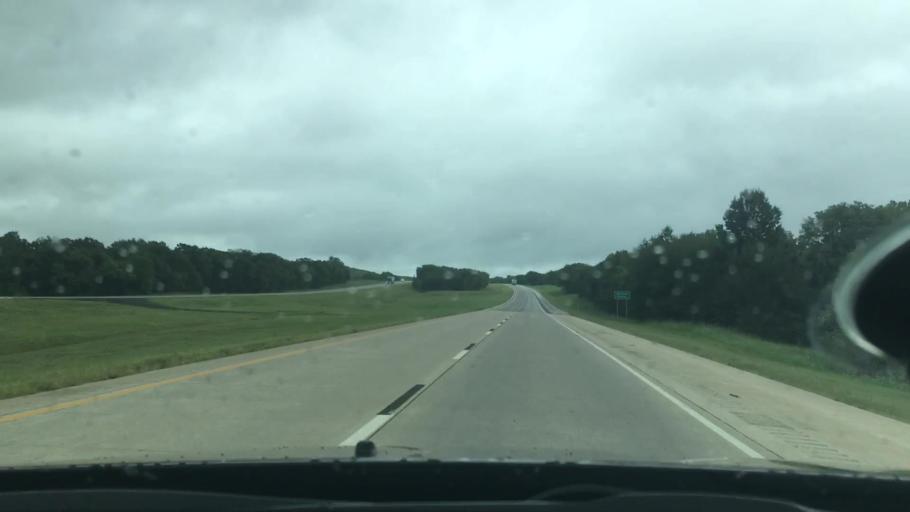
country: US
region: Oklahoma
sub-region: Okmulgee County
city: Henryetta
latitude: 35.4319
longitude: -95.8768
